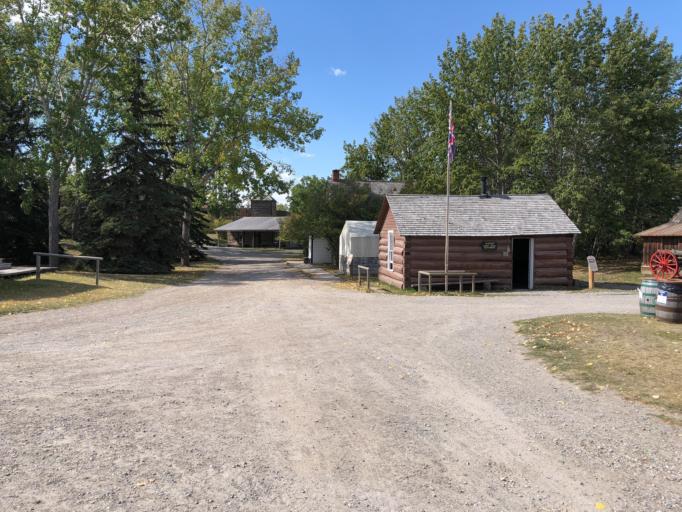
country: CA
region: Alberta
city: Calgary
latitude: 50.9869
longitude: -114.1029
